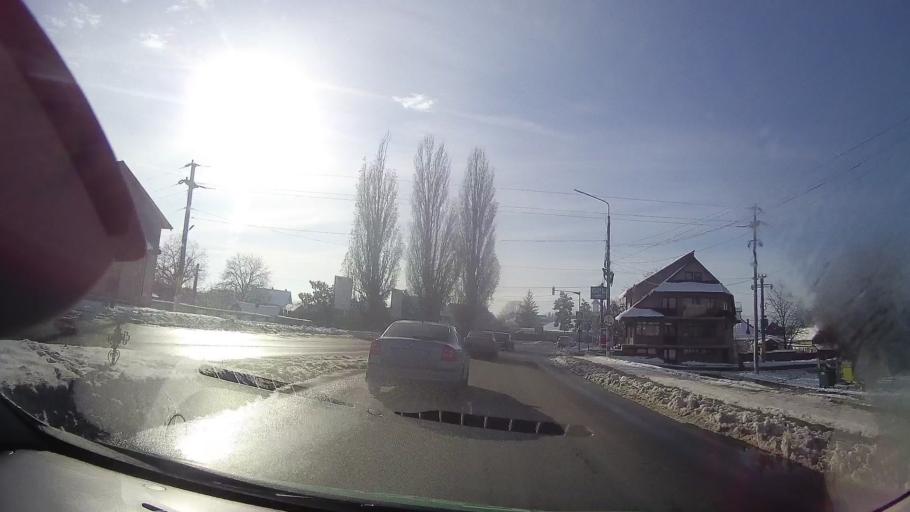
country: RO
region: Neamt
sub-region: Oras Targu Neamt
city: Humulesti
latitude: 47.2005
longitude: 26.3564
